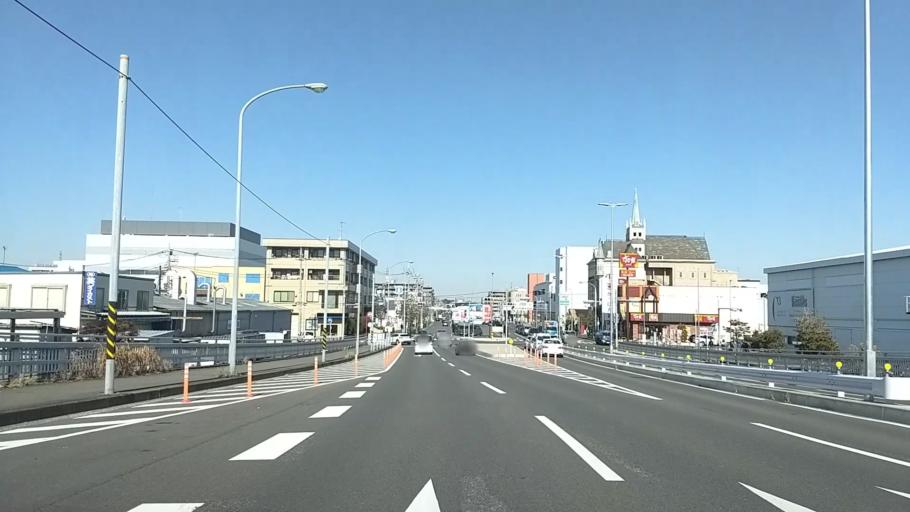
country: JP
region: Kanagawa
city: Yokohama
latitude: 35.5154
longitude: 139.6130
